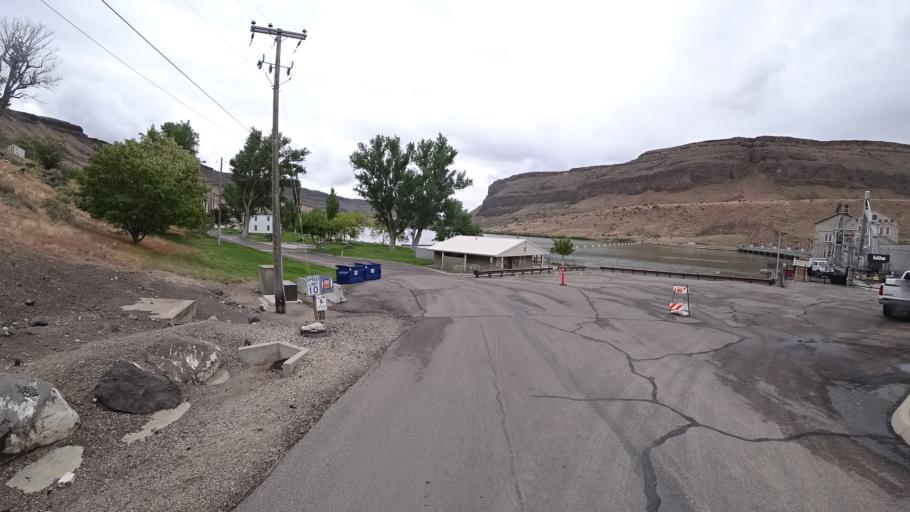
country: US
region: Idaho
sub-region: Owyhee County
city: Murphy
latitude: 43.2441
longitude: -116.3771
